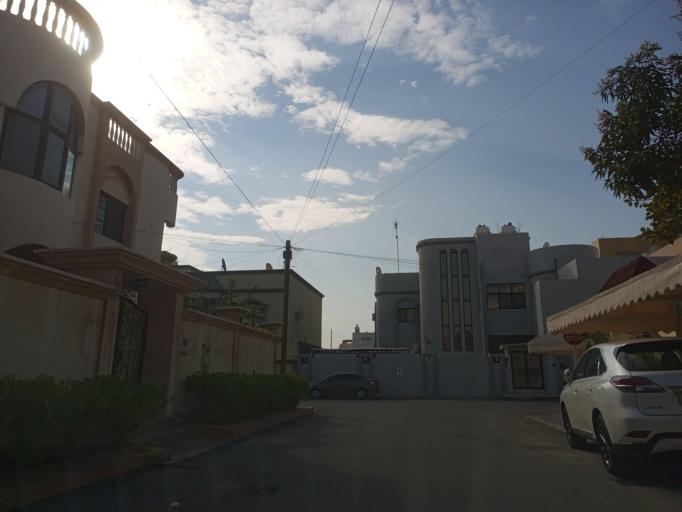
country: BH
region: Muharraq
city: Al Hadd
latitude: 26.2483
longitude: 50.6424
